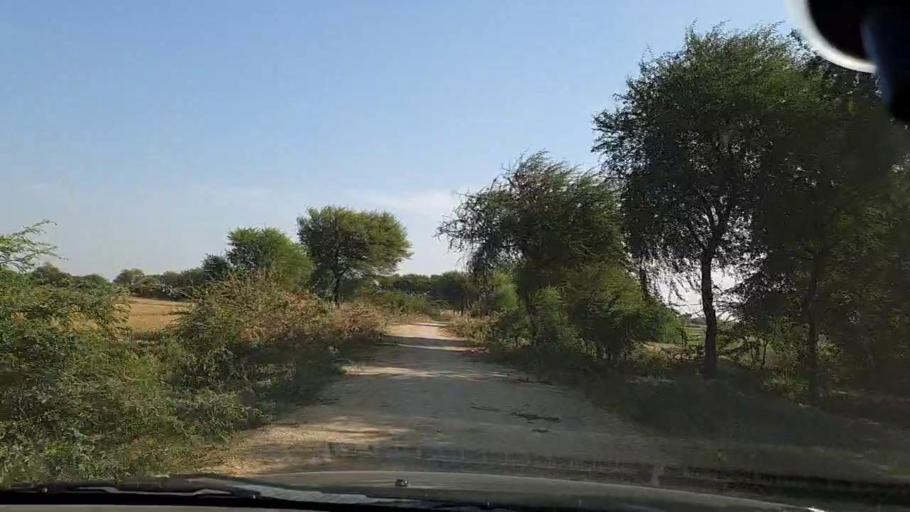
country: PK
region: Sindh
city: Mirpur Batoro
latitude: 24.6318
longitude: 68.2637
